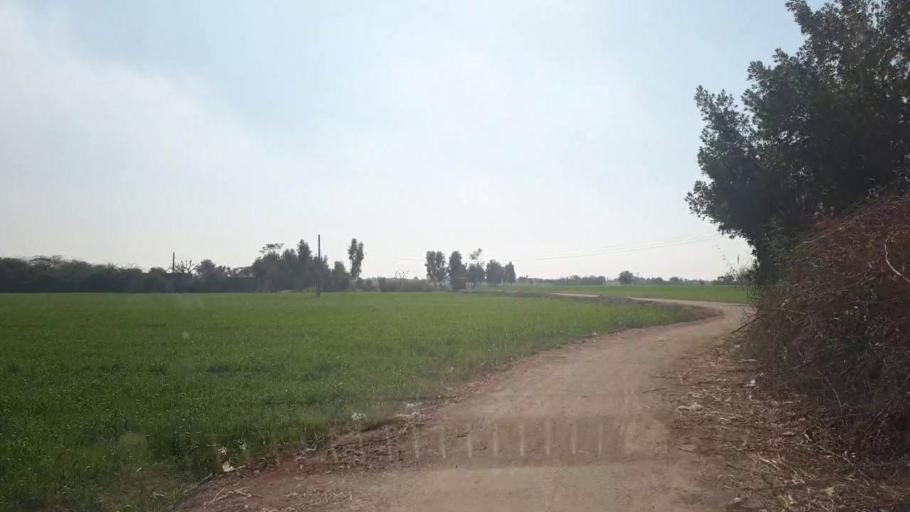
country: PK
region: Sindh
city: Shahdadpur
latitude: 25.9146
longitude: 68.5725
